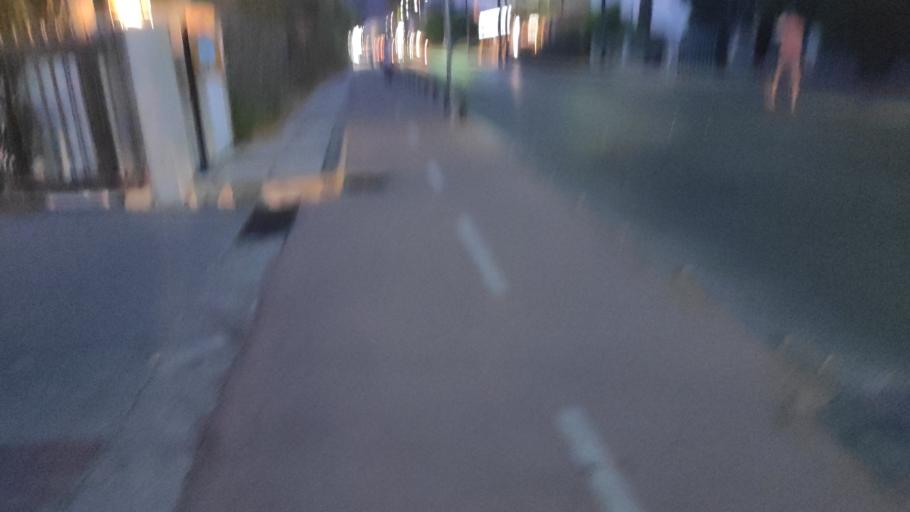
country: GR
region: South Aegean
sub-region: Nomos Dodekanisou
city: Kos
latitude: 36.9043
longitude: 27.2815
